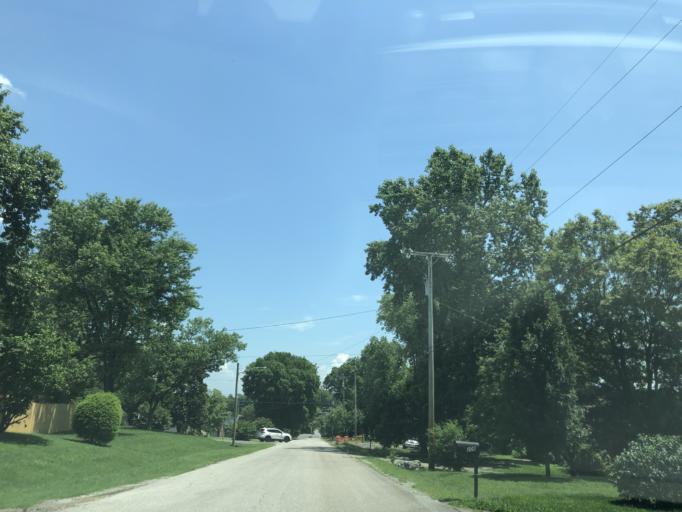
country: US
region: Tennessee
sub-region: Davidson County
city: Lakewood
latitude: 36.1750
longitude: -86.6516
